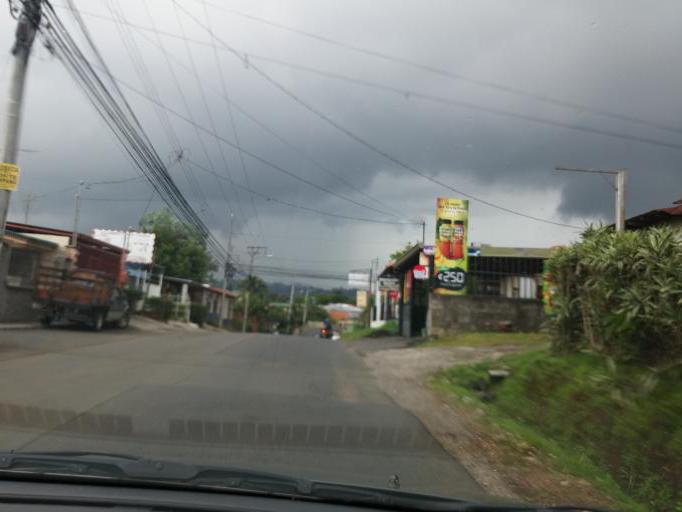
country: CR
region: Heredia
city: Llorente
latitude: 10.0199
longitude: -84.1558
